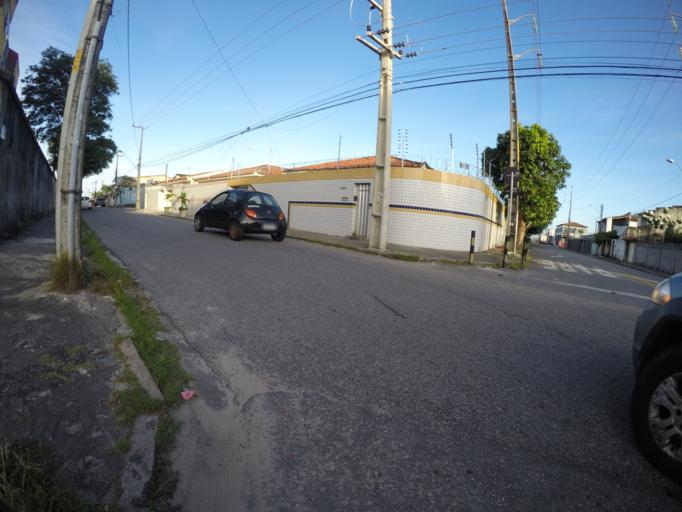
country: BR
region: Ceara
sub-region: Fortaleza
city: Fortaleza
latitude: -3.7571
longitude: -38.5129
